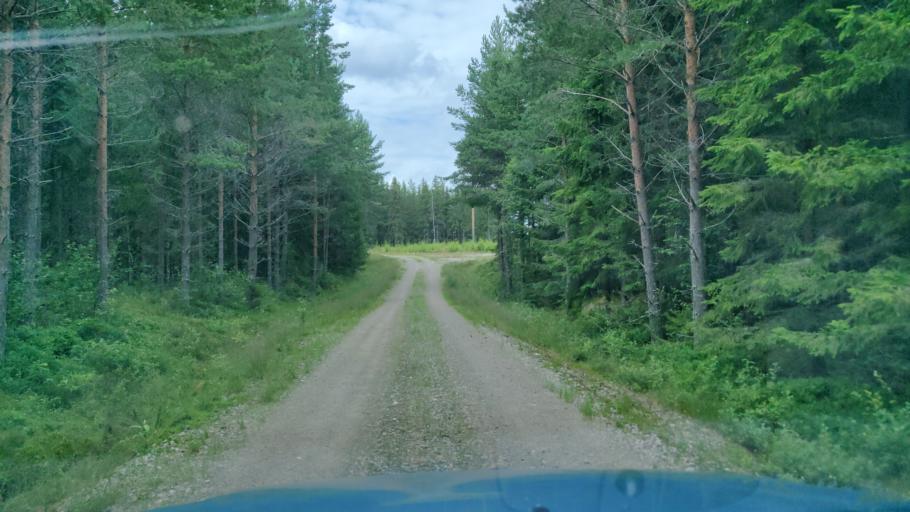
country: SE
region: Vaermland
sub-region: Hagfors Kommun
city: Hagfors
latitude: 59.9599
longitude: 13.5893
